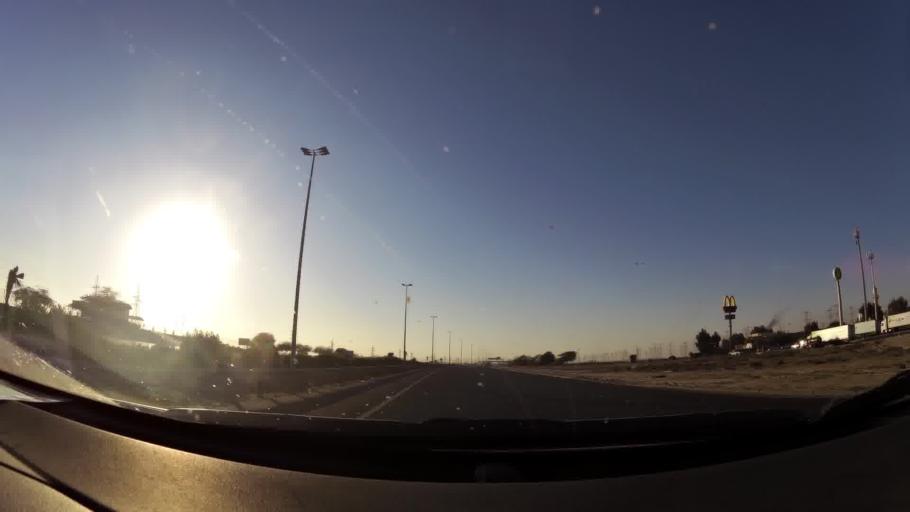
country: KW
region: Al Ahmadi
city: Al Fahahil
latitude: 28.7984
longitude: 48.2710
